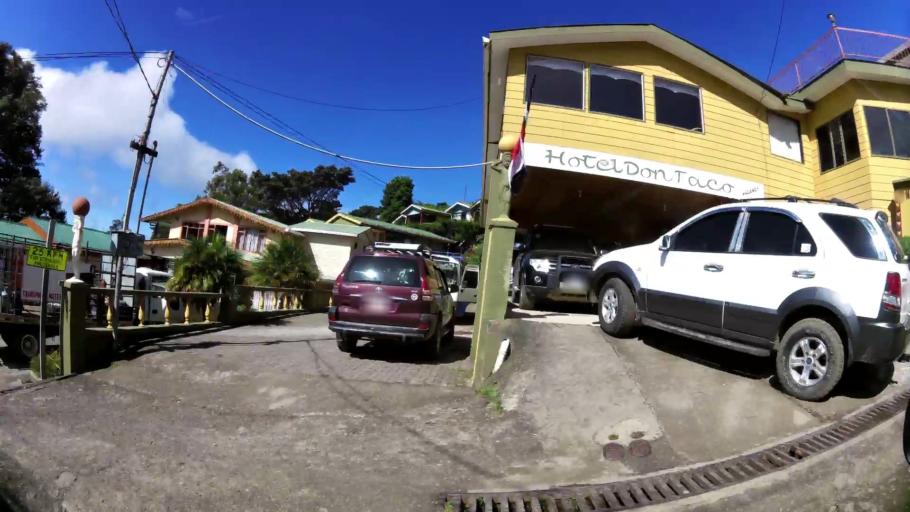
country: CR
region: Guanacaste
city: Juntas
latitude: 10.3208
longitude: -84.8230
